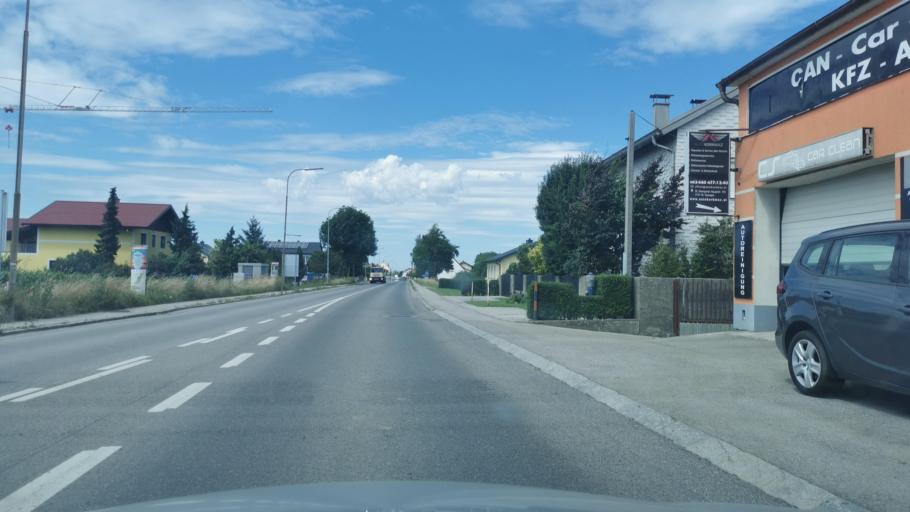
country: AT
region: Lower Austria
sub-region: Politischer Bezirk Sankt Polten
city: Wilhelmsburg
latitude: 48.1327
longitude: 15.6129
